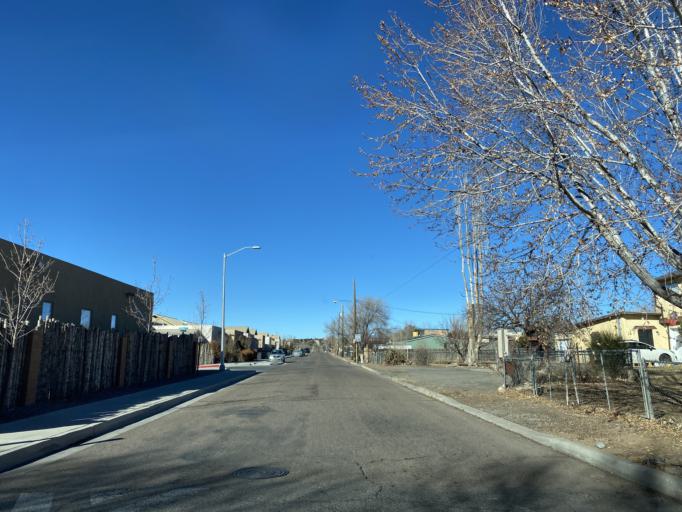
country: US
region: New Mexico
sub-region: Santa Fe County
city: Agua Fria
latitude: 35.6635
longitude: -105.9892
